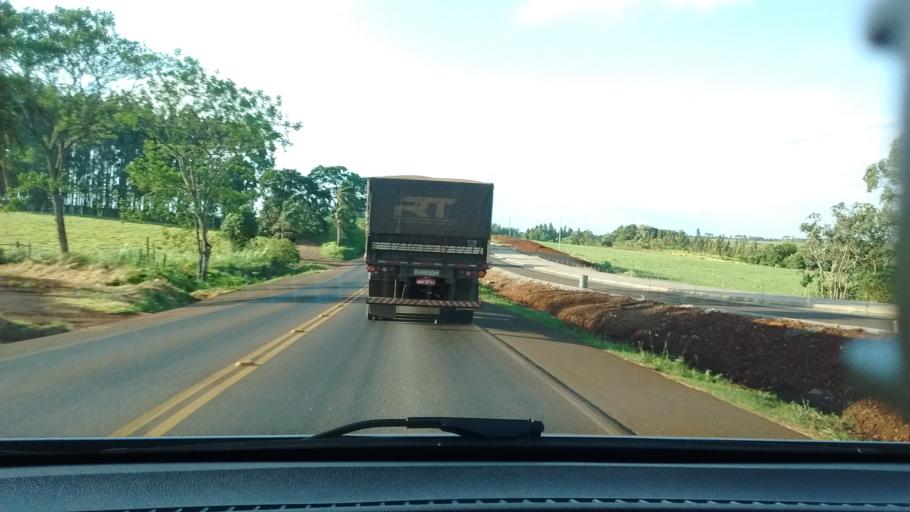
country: BR
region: Parana
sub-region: Cascavel
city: Cascavel
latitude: -25.1591
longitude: -53.5975
